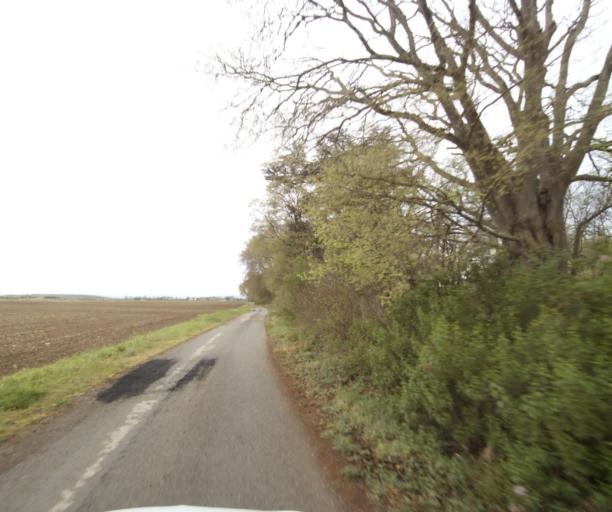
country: FR
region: Midi-Pyrenees
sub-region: Departement de la Haute-Garonne
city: Calmont
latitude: 43.2361
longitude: 1.6281
